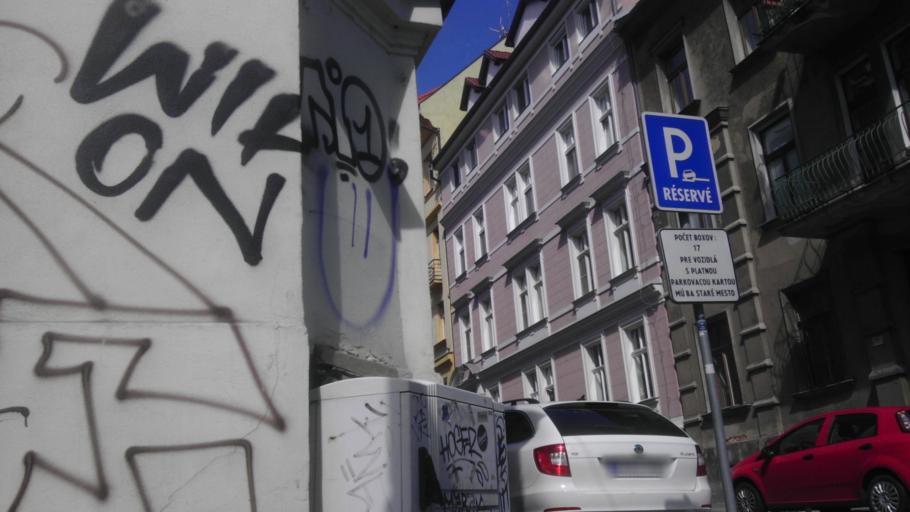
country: SK
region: Bratislavsky
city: Bratislava
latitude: 48.1543
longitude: 17.1081
